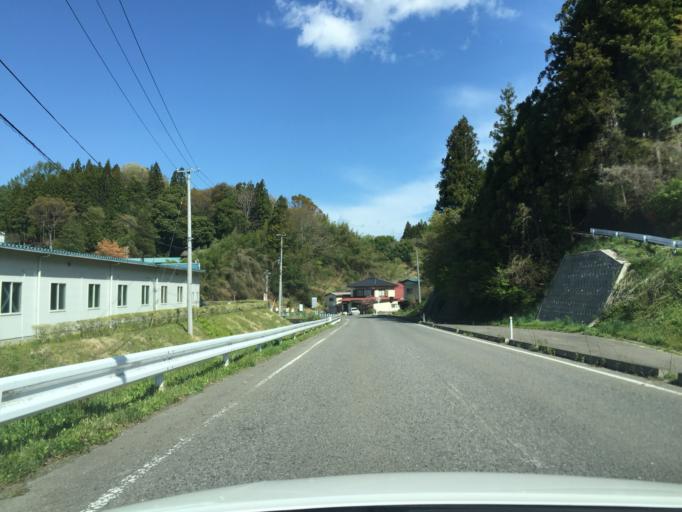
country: JP
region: Fukushima
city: Funehikimachi-funehiki
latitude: 37.5315
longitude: 140.5904
